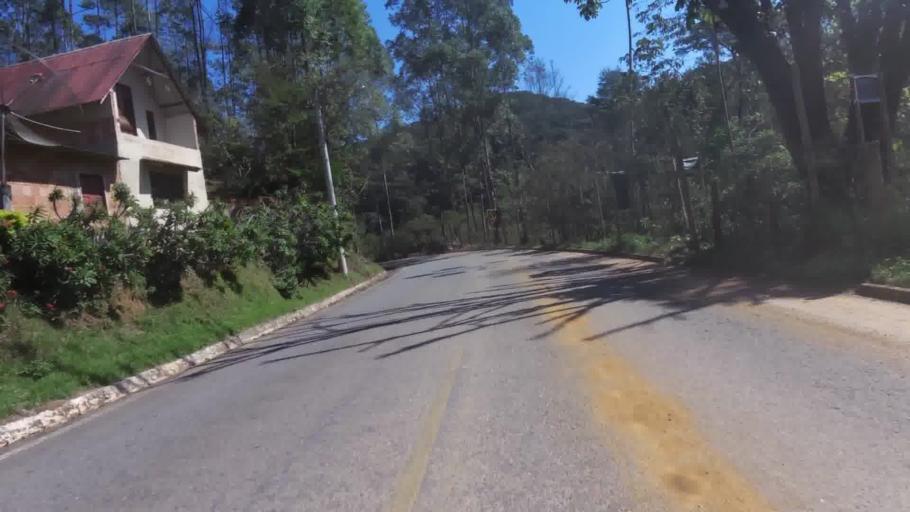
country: BR
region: Espirito Santo
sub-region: Alfredo Chaves
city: Alfredo Chaves
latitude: -20.5596
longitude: -40.8159
